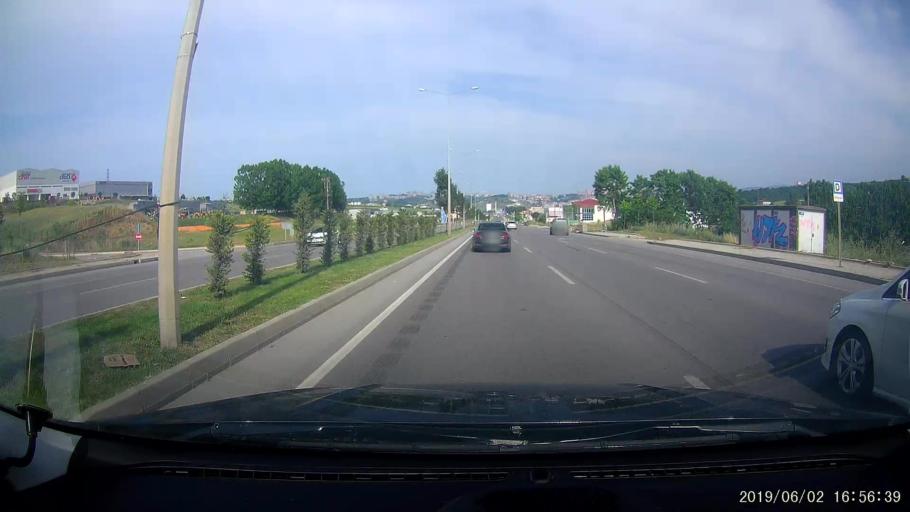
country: TR
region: Samsun
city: Samsun
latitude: 41.2922
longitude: 36.2631
